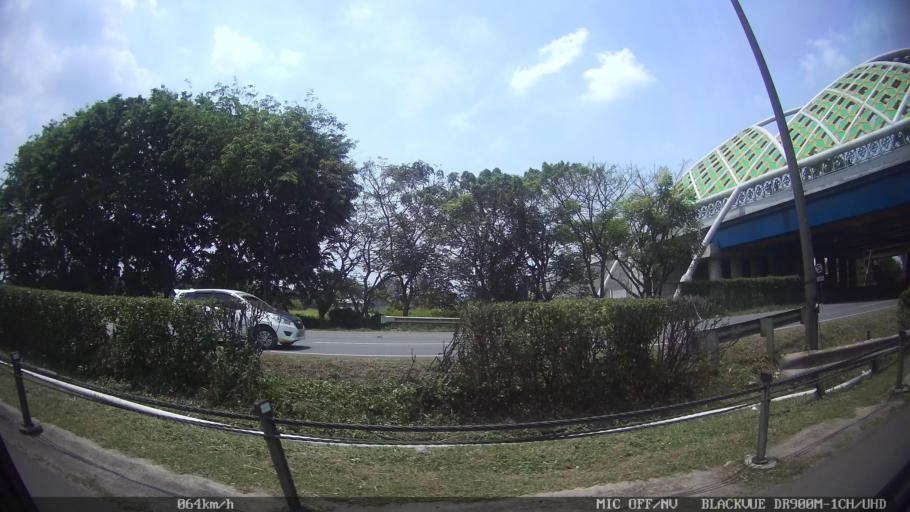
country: ID
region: Banten
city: Serang
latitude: -6.1311
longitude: 106.2014
